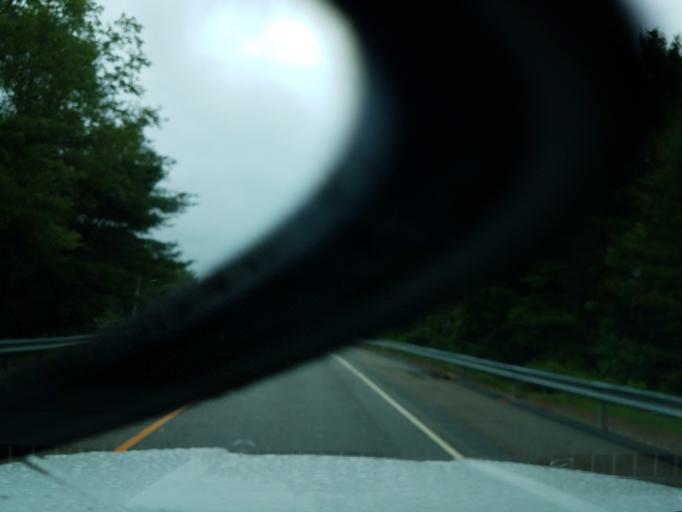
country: US
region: Rhode Island
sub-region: Providence County
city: Foster
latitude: 41.7916
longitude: -71.7970
